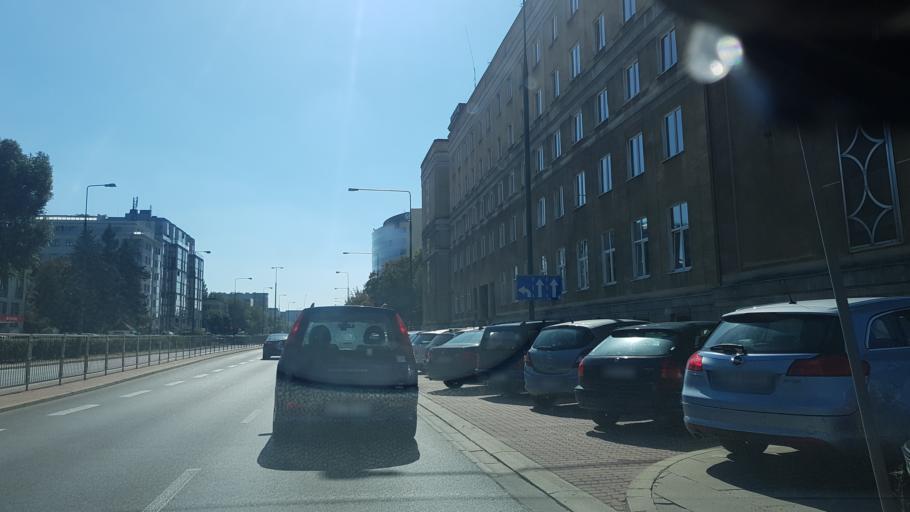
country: PL
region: Masovian Voivodeship
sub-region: Warszawa
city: Mokotow
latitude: 52.1928
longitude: 21.0151
